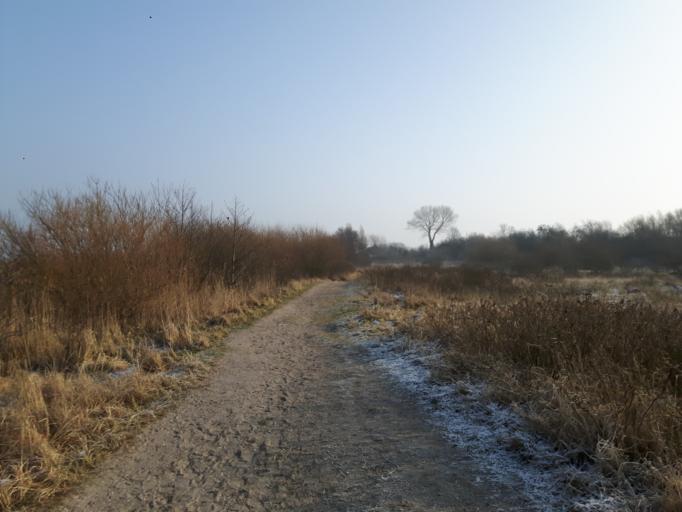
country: DE
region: Schleswig-Holstein
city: Laboe
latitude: 54.4150
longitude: 10.2348
